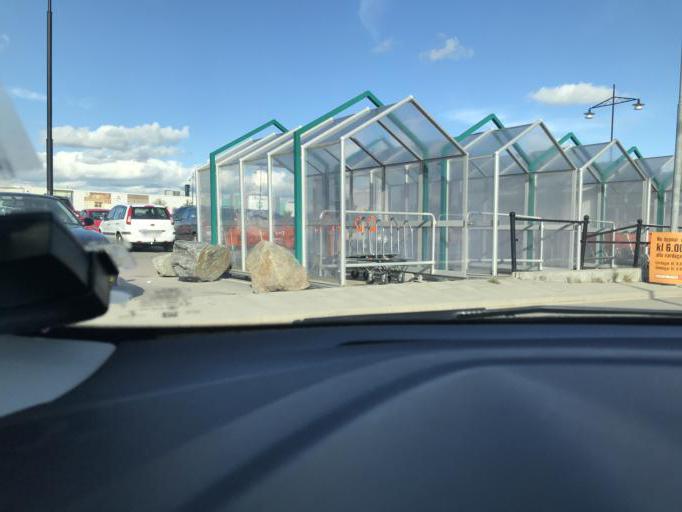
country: SE
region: Stockholm
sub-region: Botkyrka Kommun
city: Fittja
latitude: 59.2528
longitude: 17.8627
